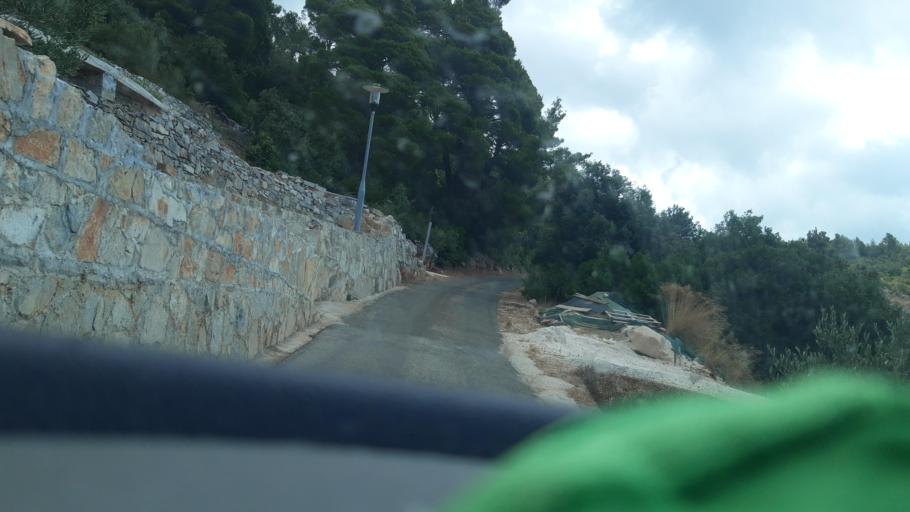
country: HR
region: Dubrovacko-Neretvanska
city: Blato
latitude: 42.7550
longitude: 17.4657
